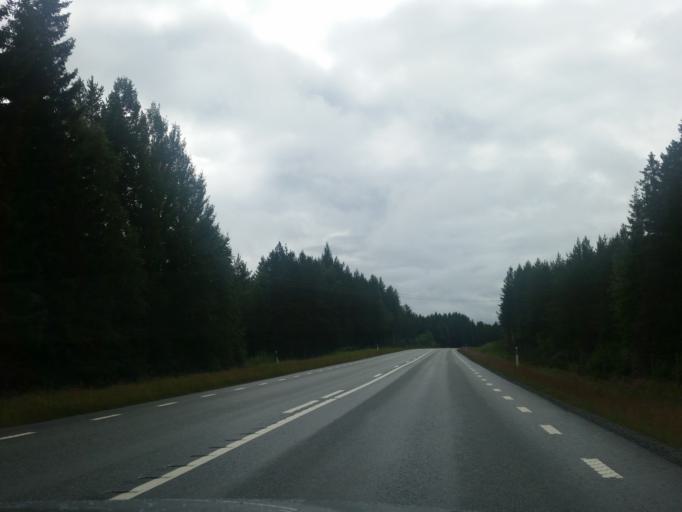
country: SE
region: Vaesterbotten
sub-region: Robertsfors Kommun
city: Robertsfors
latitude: 64.0274
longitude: 20.8415
